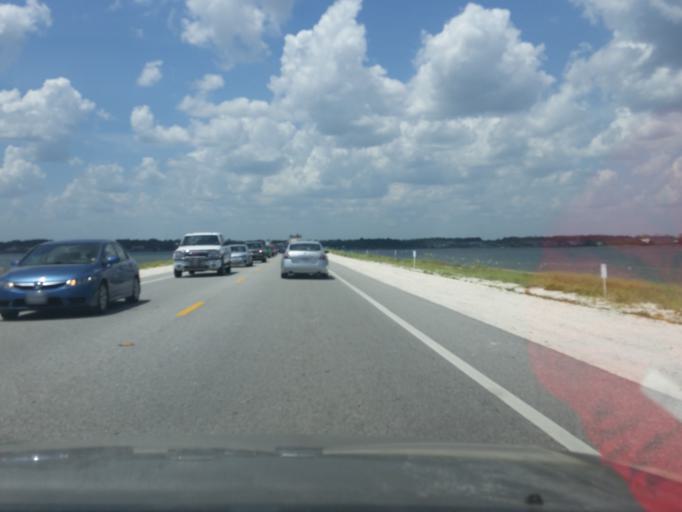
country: US
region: Florida
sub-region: Santa Rosa County
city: Navarre
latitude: 30.3898
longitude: -86.8627
